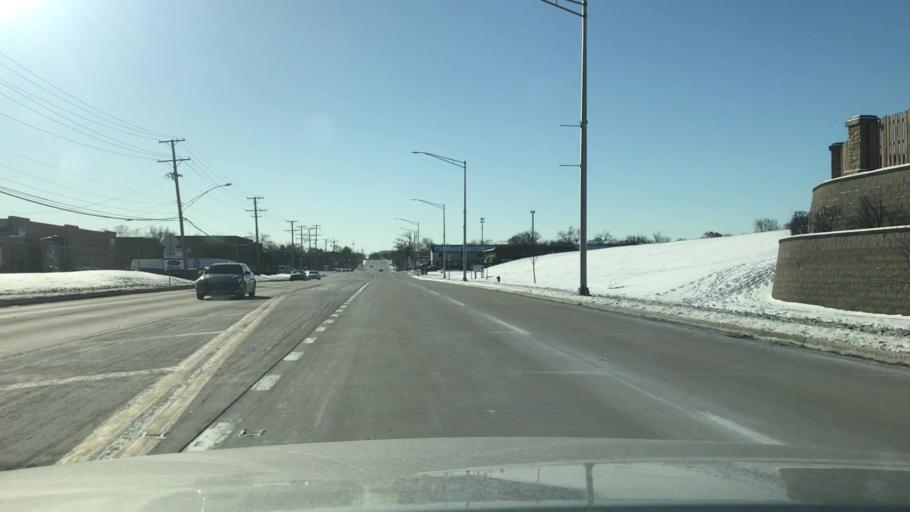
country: US
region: Illinois
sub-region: Cook County
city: Justice
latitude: 41.7421
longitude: -87.8384
